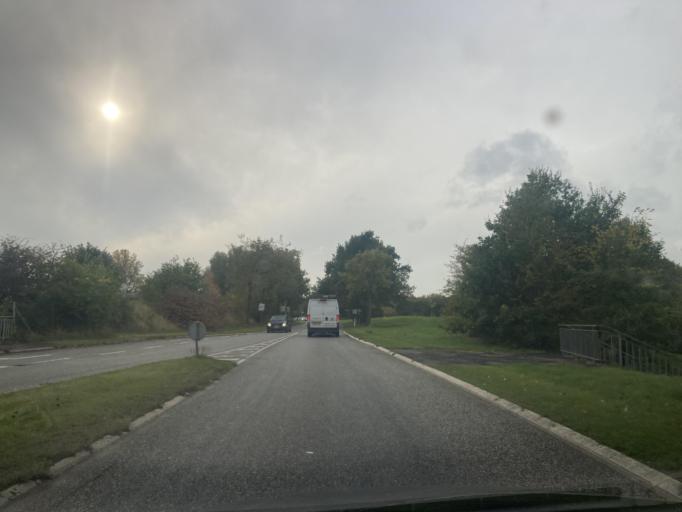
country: DK
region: Capital Region
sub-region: Herlev Kommune
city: Herlev
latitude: 55.7441
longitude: 12.4139
